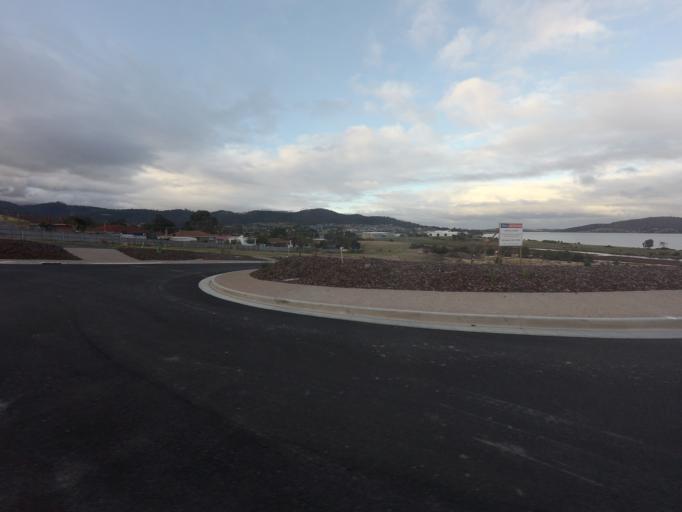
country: AU
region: Tasmania
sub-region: Clarence
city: Rokeby
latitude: -42.9066
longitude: 147.4298
